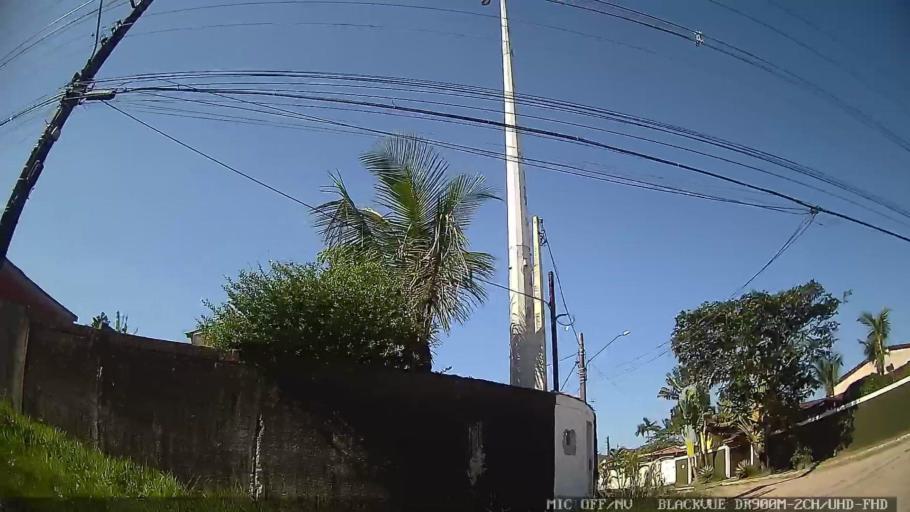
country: BR
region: Sao Paulo
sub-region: Guaruja
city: Guaruja
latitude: -23.9737
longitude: -46.2125
